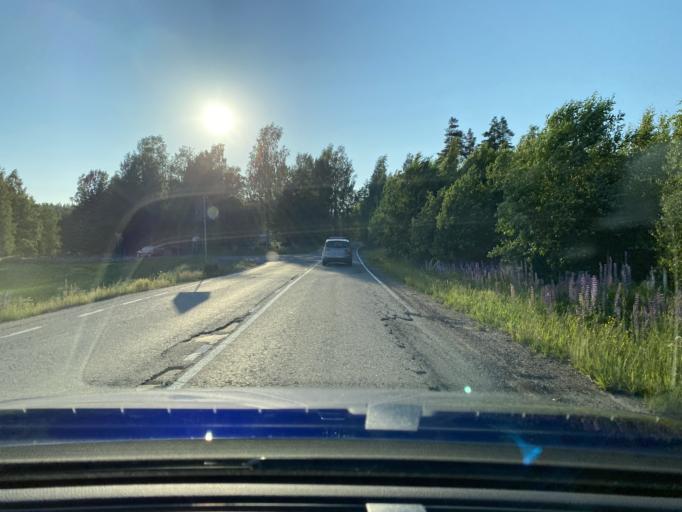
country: FI
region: Haeme
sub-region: Riihimaeki
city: Riihimaeki
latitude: 60.7186
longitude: 24.7089
